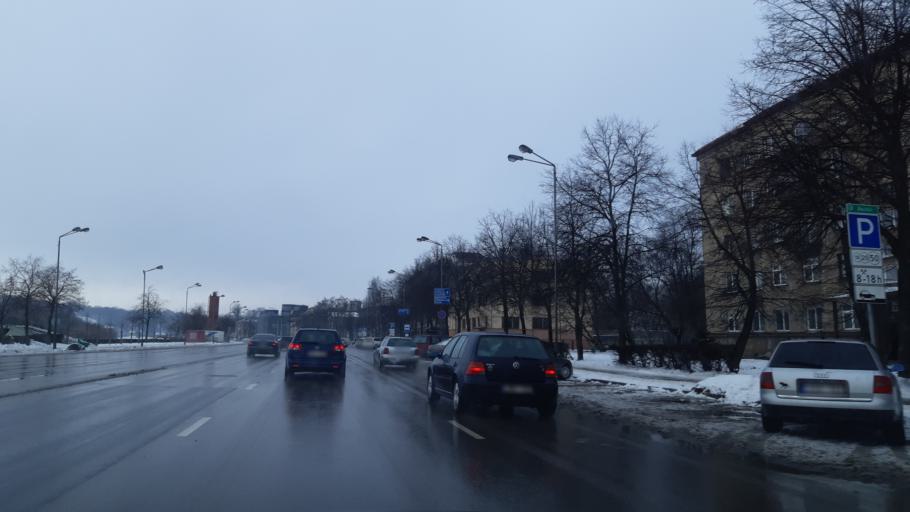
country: LT
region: Kauno apskritis
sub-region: Kaunas
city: Kaunas
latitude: 54.8946
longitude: 23.9085
